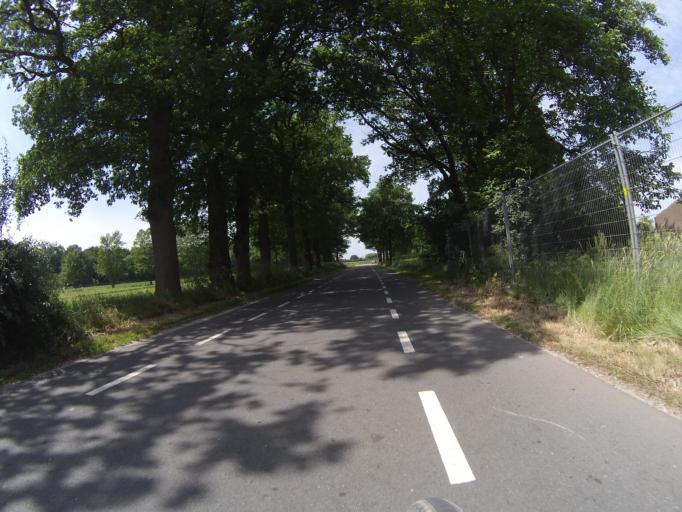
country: NL
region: Gelderland
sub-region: Gemeente Ede
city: Lunteren
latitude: 52.1055
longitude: 5.6353
